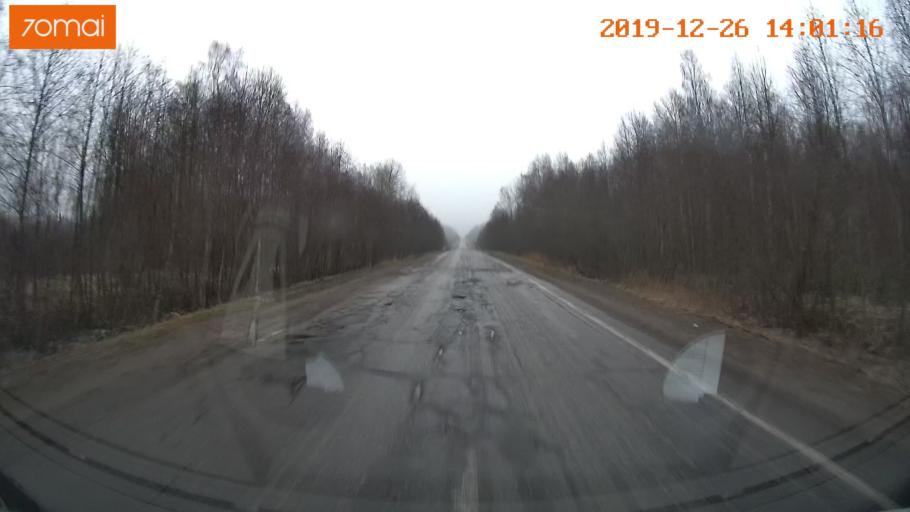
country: RU
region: Jaroslavl
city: Poshekhon'ye
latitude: 58.5517
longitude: 38.7605
